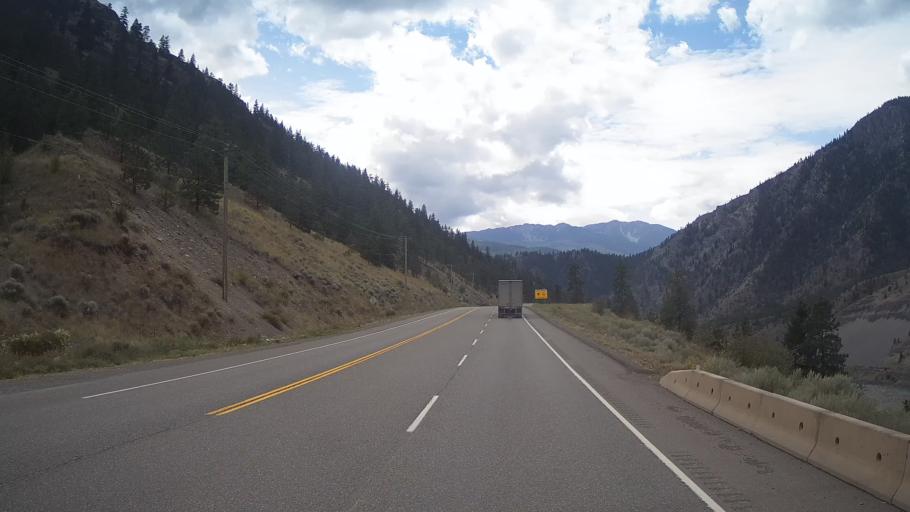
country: CA
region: British Columbia
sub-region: Thompson-Nicola Regional District
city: Ashcroft
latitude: 50.2944
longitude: -121.3923
